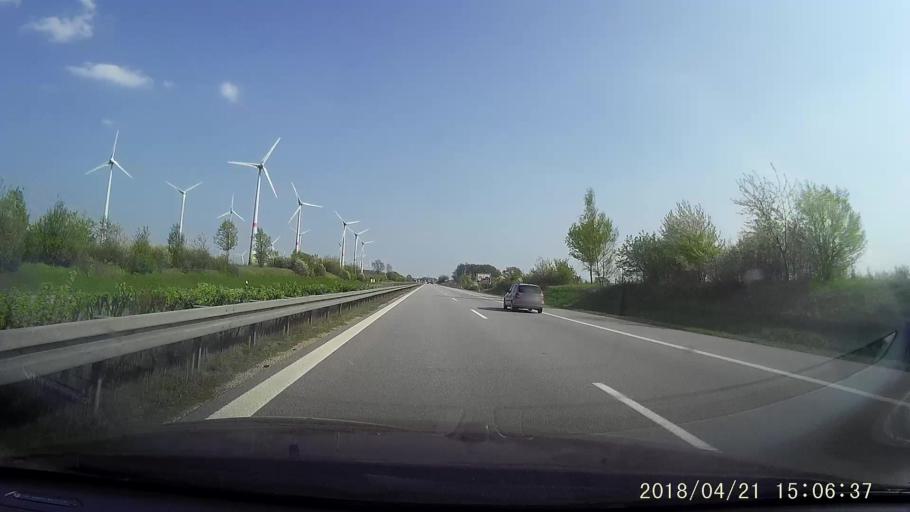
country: DE
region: Saxony
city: Kodersdorf
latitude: 51.2106
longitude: 14.9402
